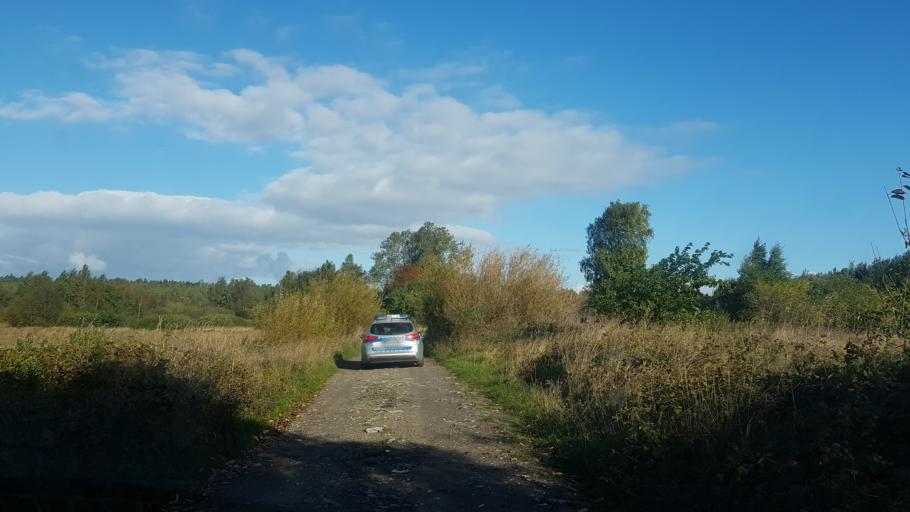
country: PL
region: West Pomeranian Voivodeship
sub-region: Powiat kolobrzeski
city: Grzybowo
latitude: 54.1661
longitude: 15.5162
